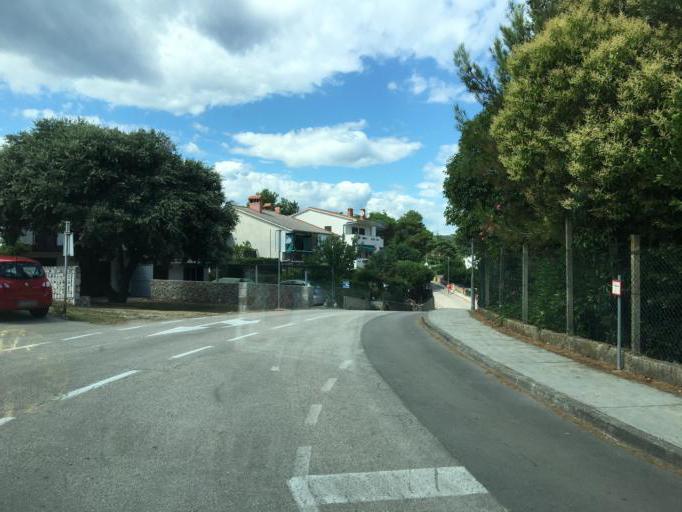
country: HR
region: Primorsko-Goranska
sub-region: Grad Krk
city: Krk
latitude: 45.0193
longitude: 14.5662
